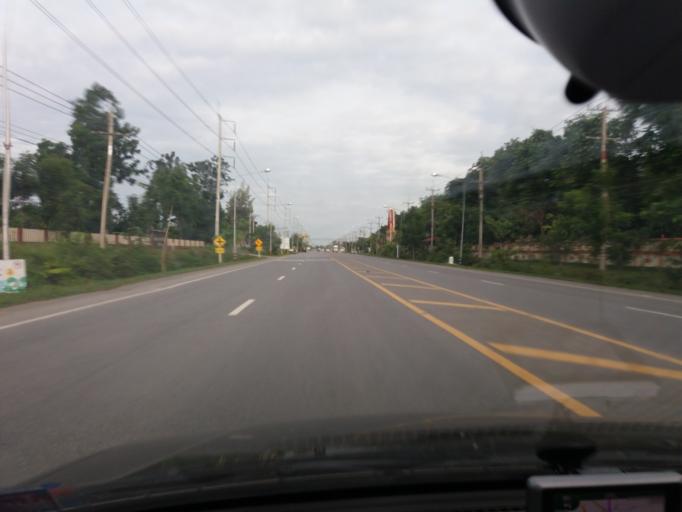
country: TH
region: Suphan Buri
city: U Thong
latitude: 14.3350
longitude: 99.7855
